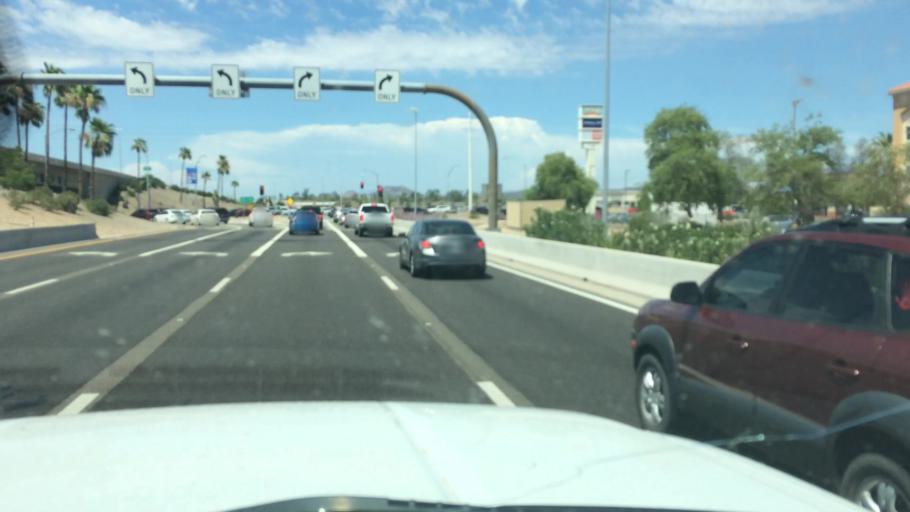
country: US
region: Arizona
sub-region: Maricopa County
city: Sun City
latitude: 33.6369
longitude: -112.2375
